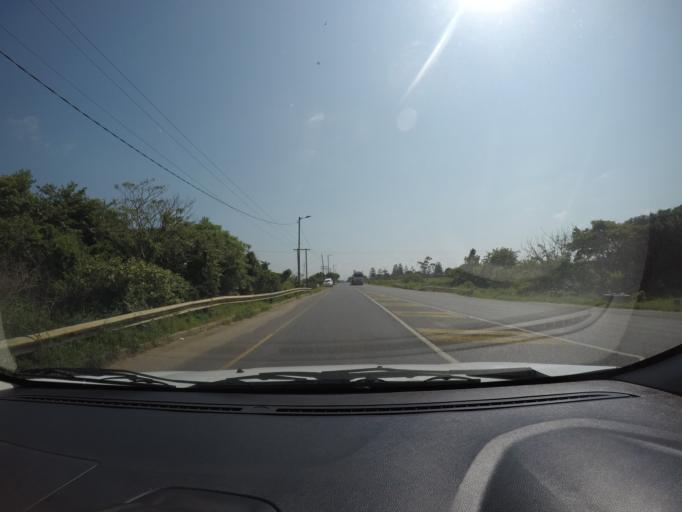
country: ZA
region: KwaZulu-Natal
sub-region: uThungulu District Municipality
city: eSikhawini
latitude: -28.8783
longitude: 31.8926
